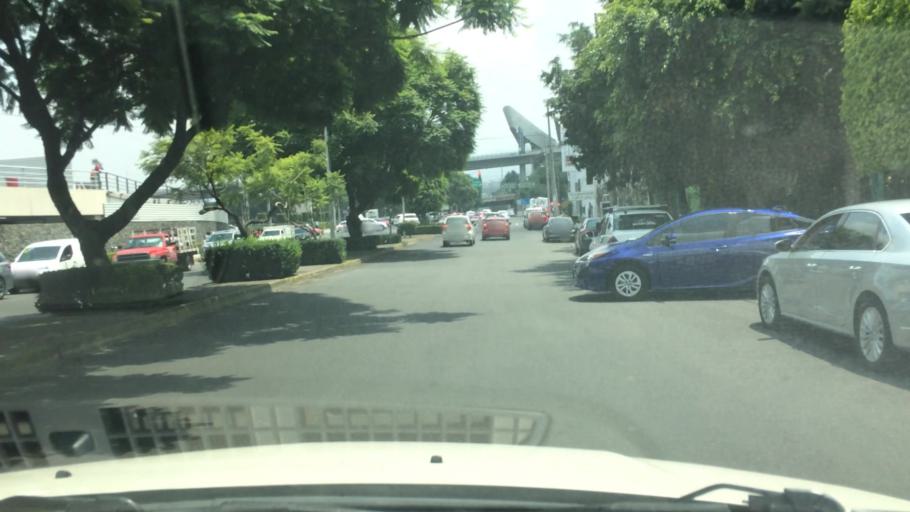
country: MX
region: Mexico City
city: Tlalpan
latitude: 19.3047
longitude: -99.1933
